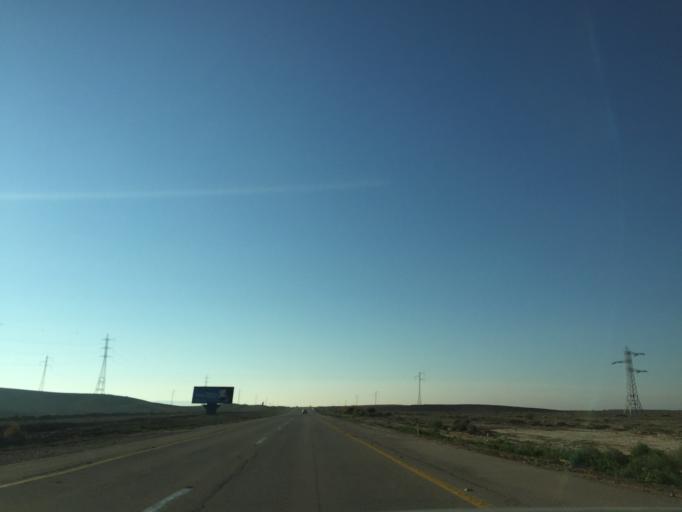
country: IL
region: Southern District
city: Mitzpe Ramon
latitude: 30.4548
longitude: 34.9361
